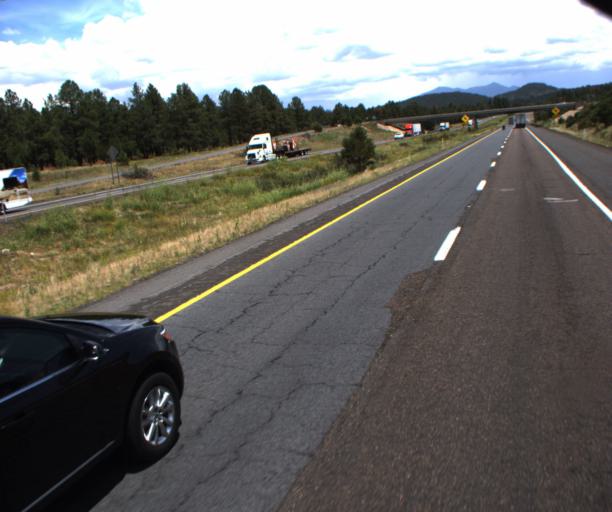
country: US
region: Arizona
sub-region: Coconino County
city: Parks
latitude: 35.2548
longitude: -111.9416
